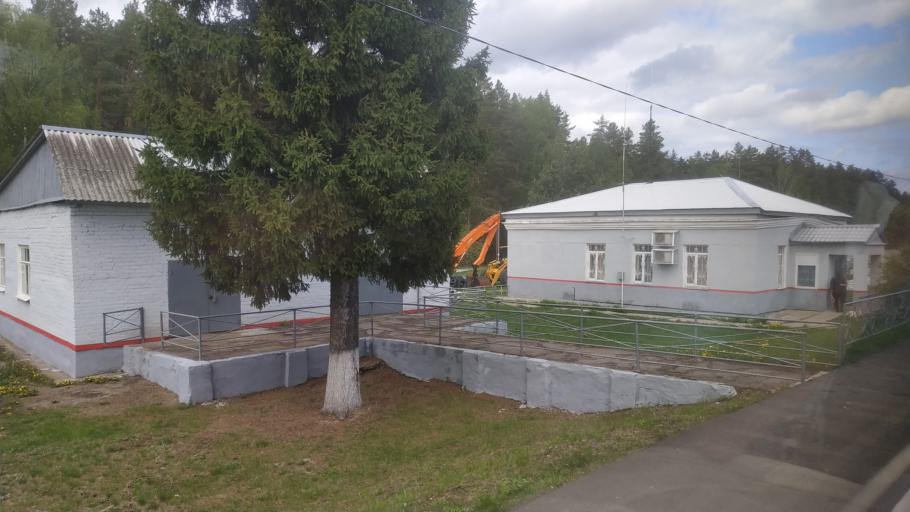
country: RU
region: Kaluga
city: Lyudinovo
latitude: 53.8312
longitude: 34.4313
